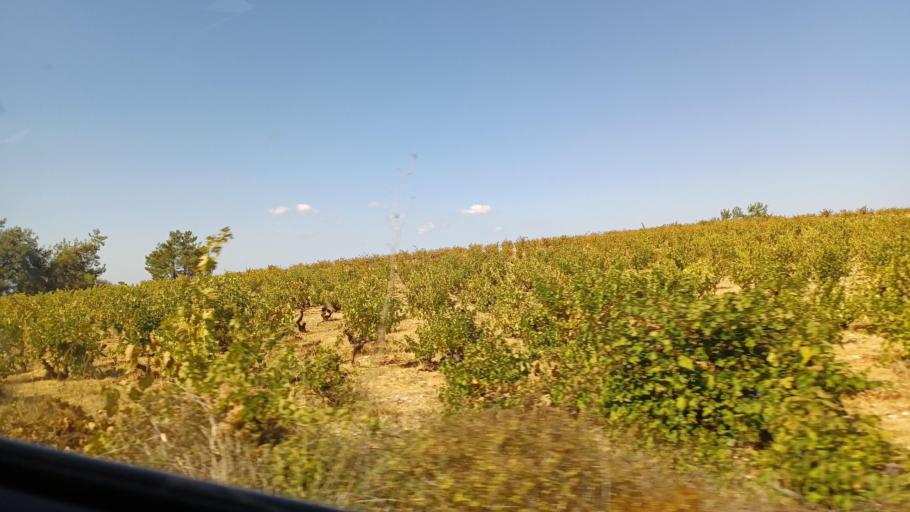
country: CY
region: Pafos
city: Mesogi
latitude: 34.9057
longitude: 32.6191
